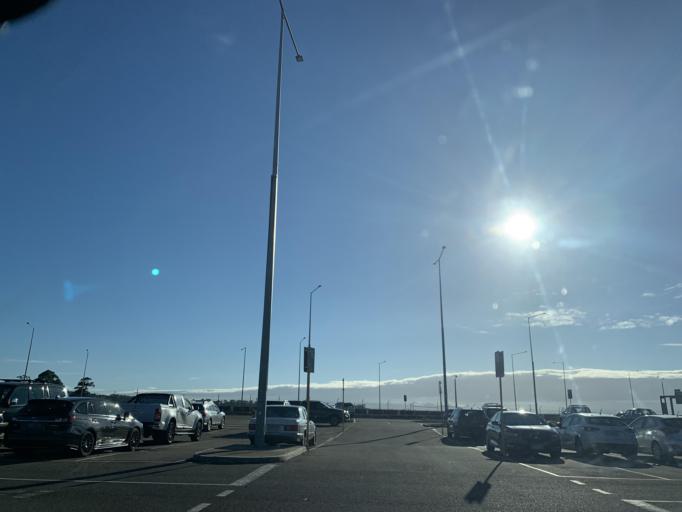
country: AU
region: Victoria
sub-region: Hume
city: Westmeadows
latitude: -37.6788
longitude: 144.8653
